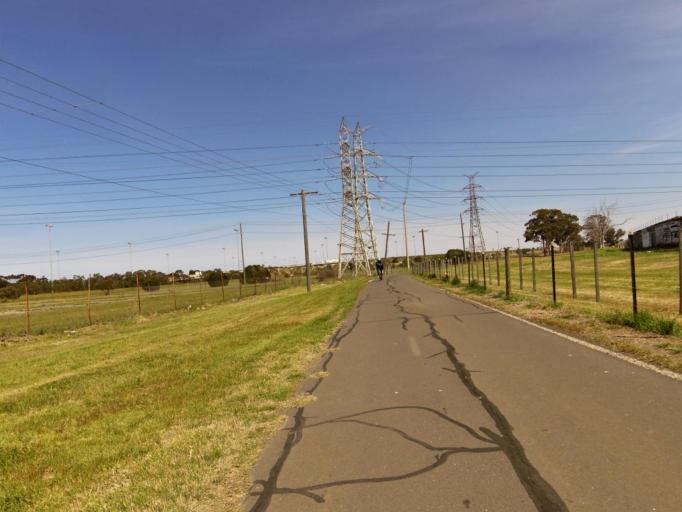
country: AU
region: Victoria
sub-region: Brimbank
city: Brooklyn
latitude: -37.8228
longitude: 144.8214
